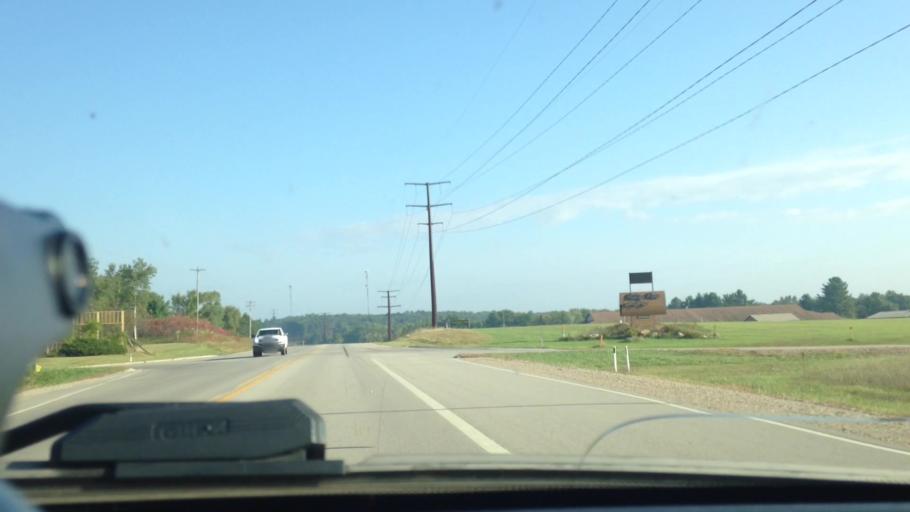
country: US
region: Wisconsin
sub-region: Marinette County
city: Peshtigo
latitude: 45.2024
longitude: -87.9943
